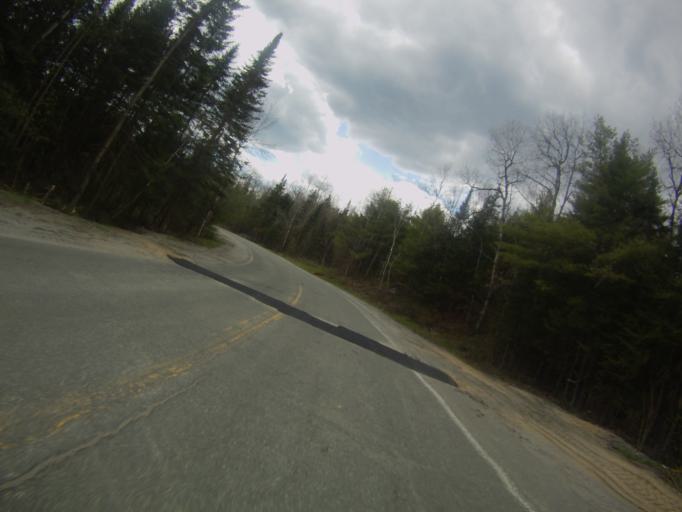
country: US
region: New York
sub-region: Essex County
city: Mineville
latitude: 44.0877
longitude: -73.5866
